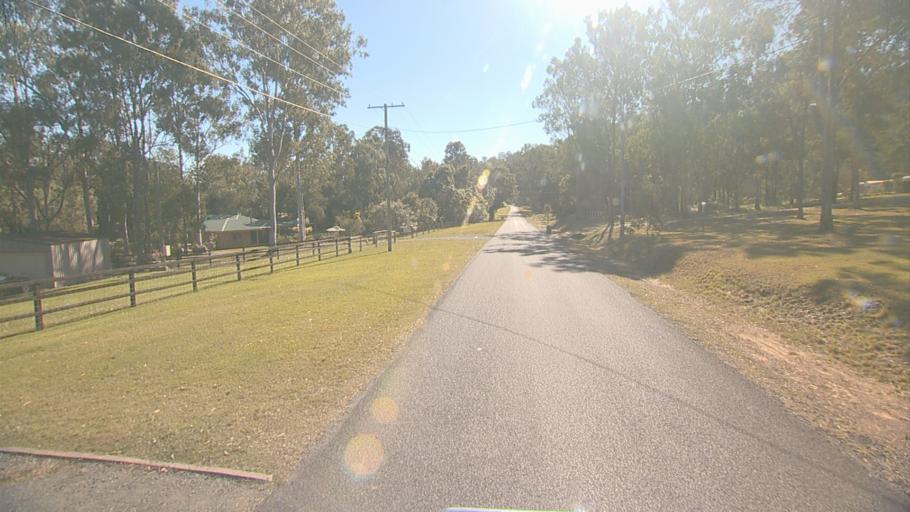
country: AU
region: Queensland
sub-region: Logan
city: Windaroo
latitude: -27.7837
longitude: 153.1477
